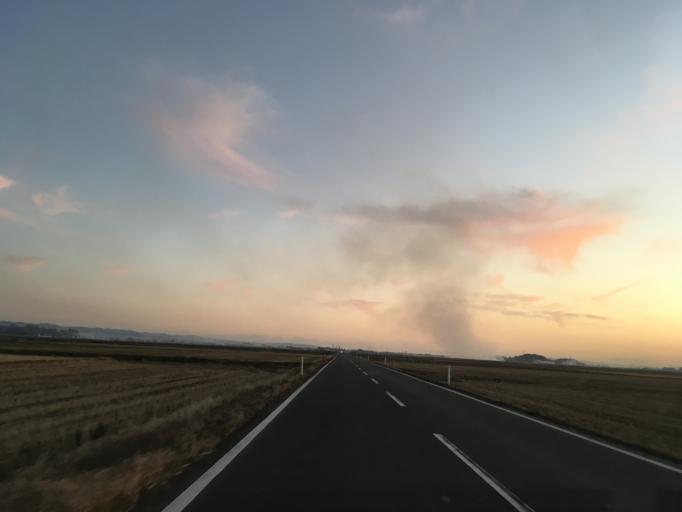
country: JP
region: Iwate
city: Ichinoseki
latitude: 38.7527
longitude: 141.2365
